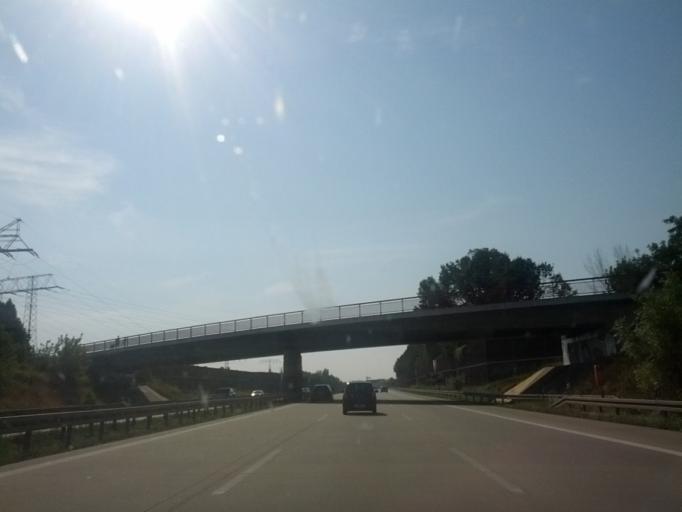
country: DE
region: Brandenburg
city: Neuenhagen
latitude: 52.5165
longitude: 13.7258
